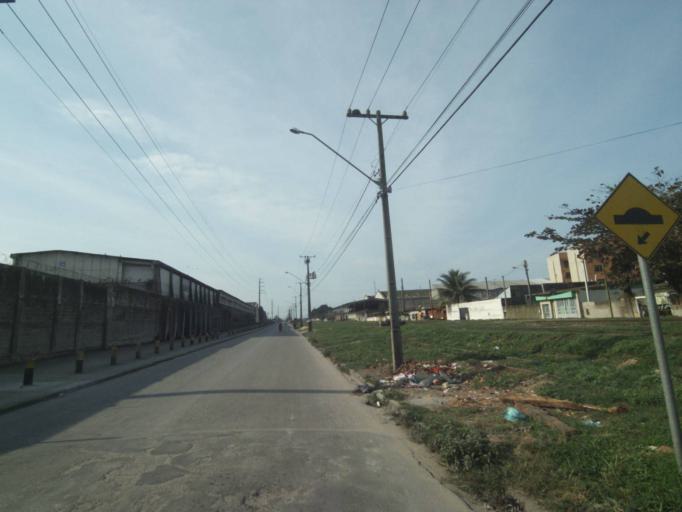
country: BR
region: Parana
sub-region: Paranagua
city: Paranagua
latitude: -25.5319
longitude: -48.5317
